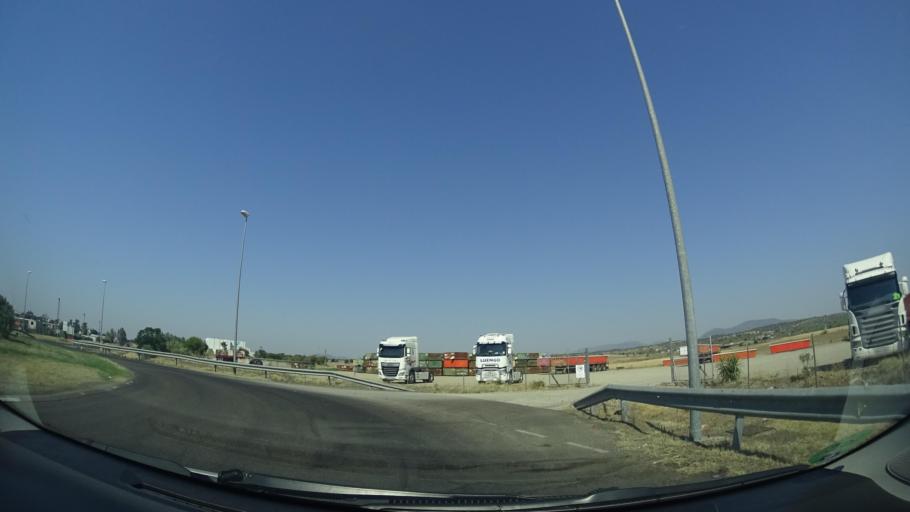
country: ES
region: Extremadura
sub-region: Provincia de Caceres
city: Miajadas
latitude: 39.1379
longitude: -5.9361
